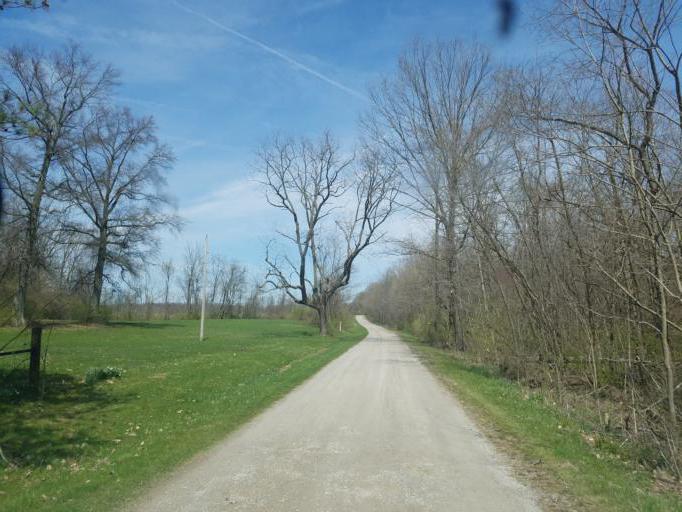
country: US
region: Ohio
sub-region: Delaware County
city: Ashley
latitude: 40.4191
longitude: -83.0589
